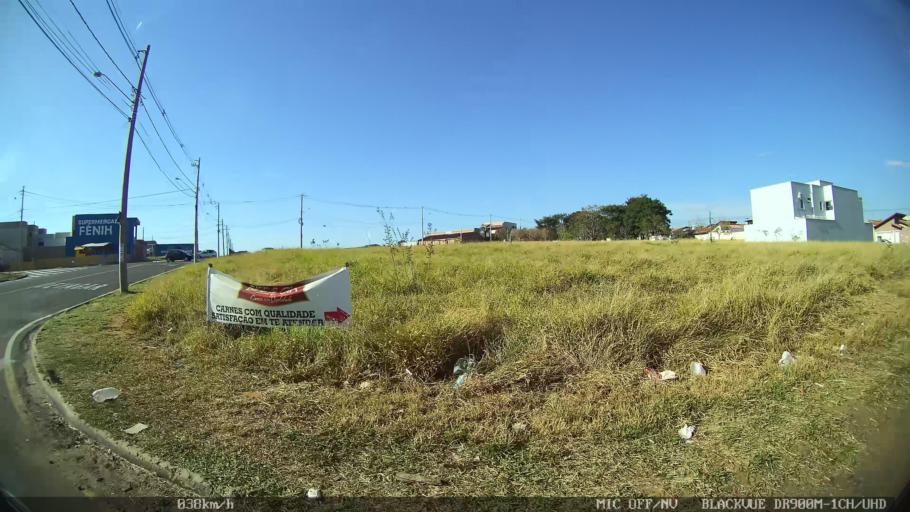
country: BR
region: Sao Paulo
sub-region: Franca
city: Franca
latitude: -20.5094
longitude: -47.4286
